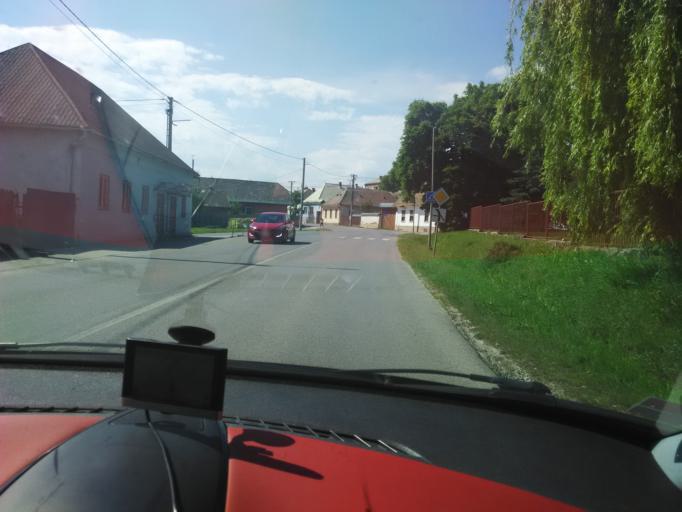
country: SK
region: Banskobystricky
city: Revuca
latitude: 48.6268
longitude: 20.2415
